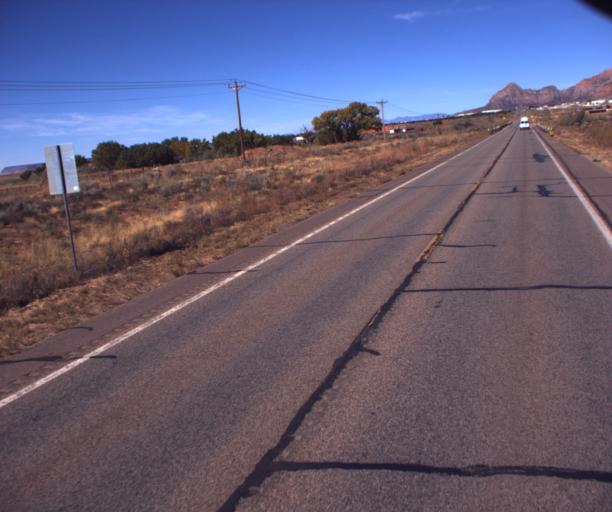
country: US
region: Arizona
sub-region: Mohave County
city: Colorado City
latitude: 36.9864
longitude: -112.9878
